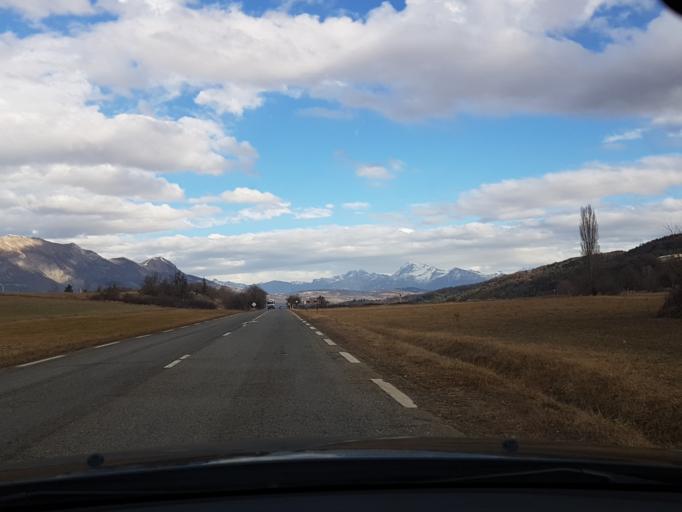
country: FR
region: Provence-Alpes-Cote d'Azur
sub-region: Departement des Hautes-Alpes
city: Tallard
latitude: 44.4922
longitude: 6.0400
